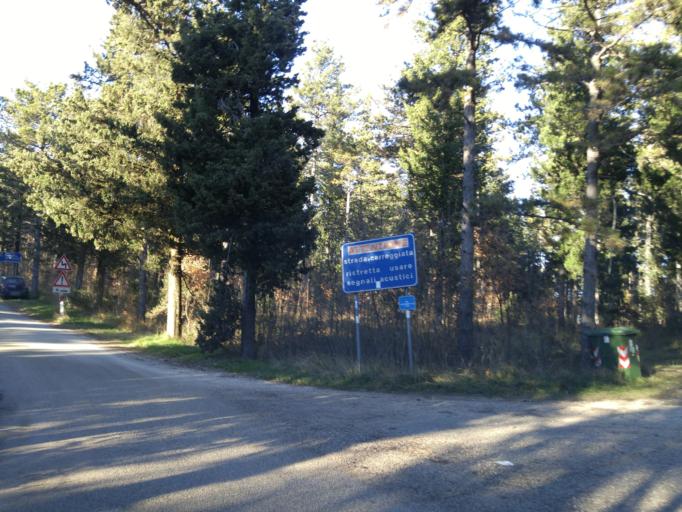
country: IT
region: The Marches
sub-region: Provincia di Pesaro e Urbino
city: Fossombrone
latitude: 43.7000
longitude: 12.7761
